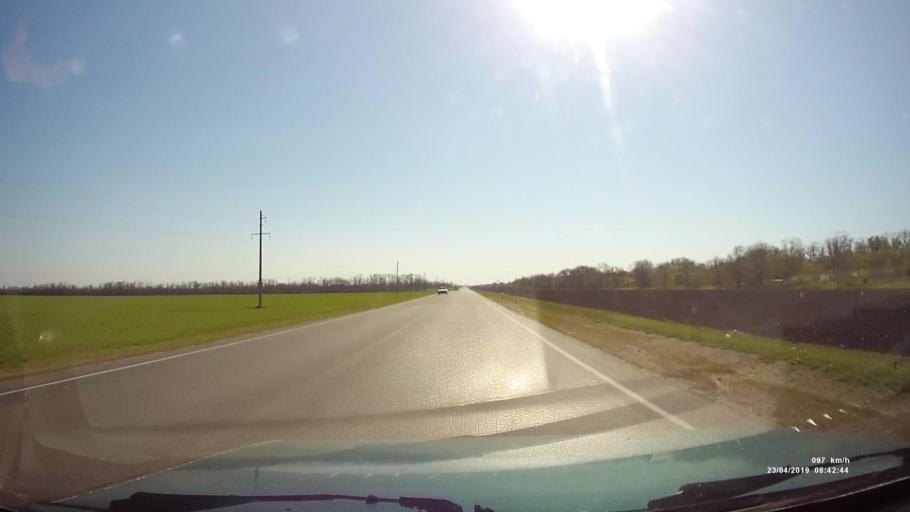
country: RU
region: Rostov
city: Gigant
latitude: 46.5228
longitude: 41.2765
